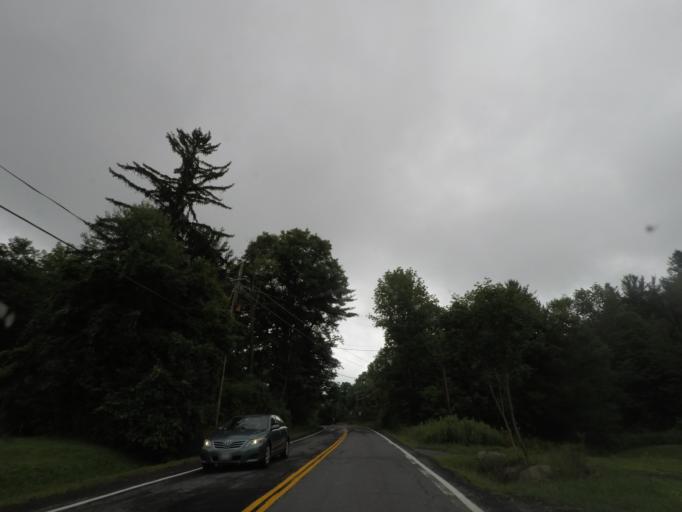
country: US
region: New York
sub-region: Rensselaer County
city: Averill Park
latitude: 42.5809
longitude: -73.4760
